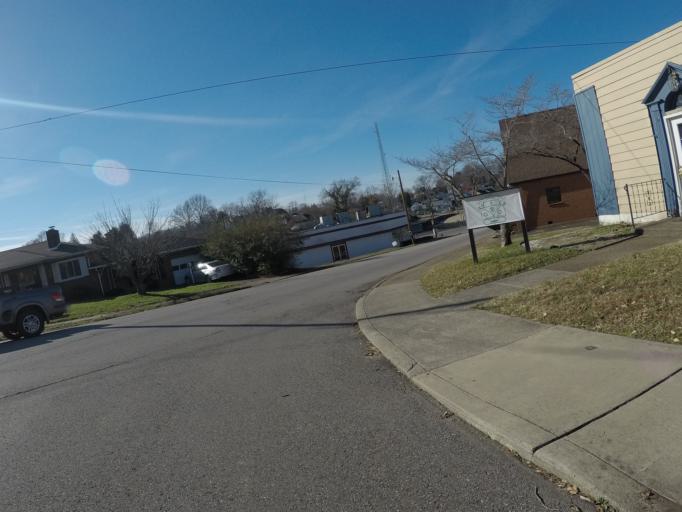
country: US
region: West Virginia
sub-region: Cabell County
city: Huntington
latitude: 38.4067
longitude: -82.4044
